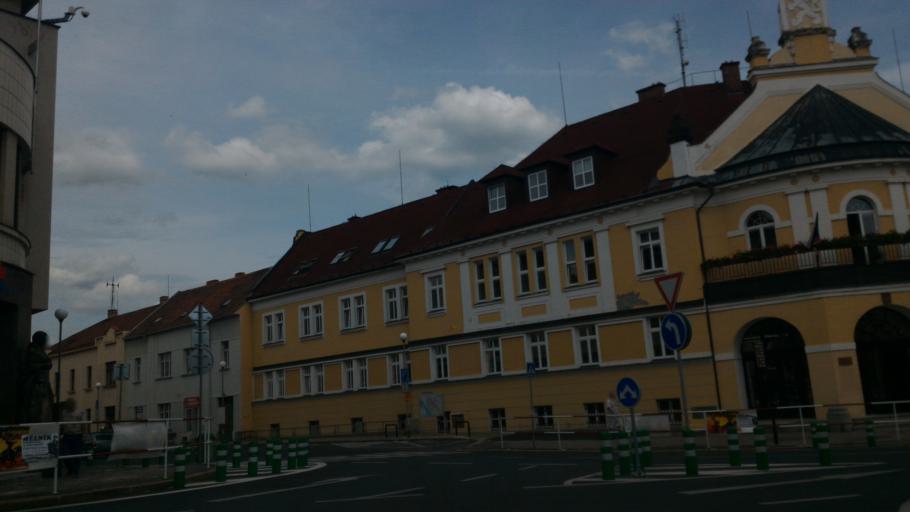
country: CZ
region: Central Bohemia
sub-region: Okres Melnik
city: Melnik
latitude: 50.3502
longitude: 14.4785
